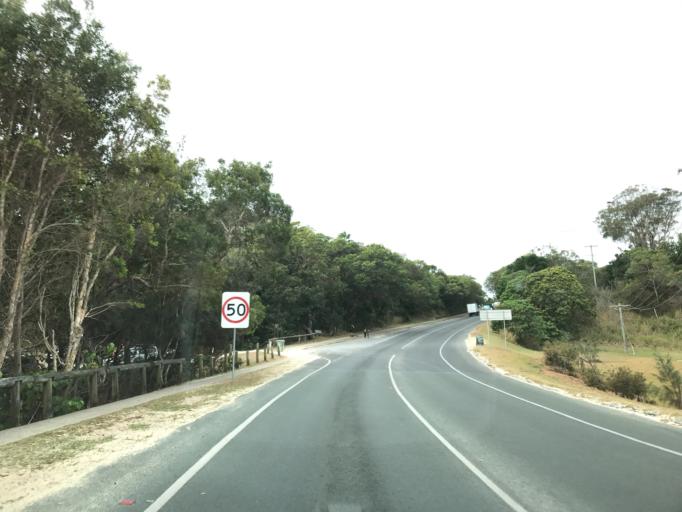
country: AU
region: Queensland
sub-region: Redland
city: Victoria Point
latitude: -27.4274
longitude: 153.5281
